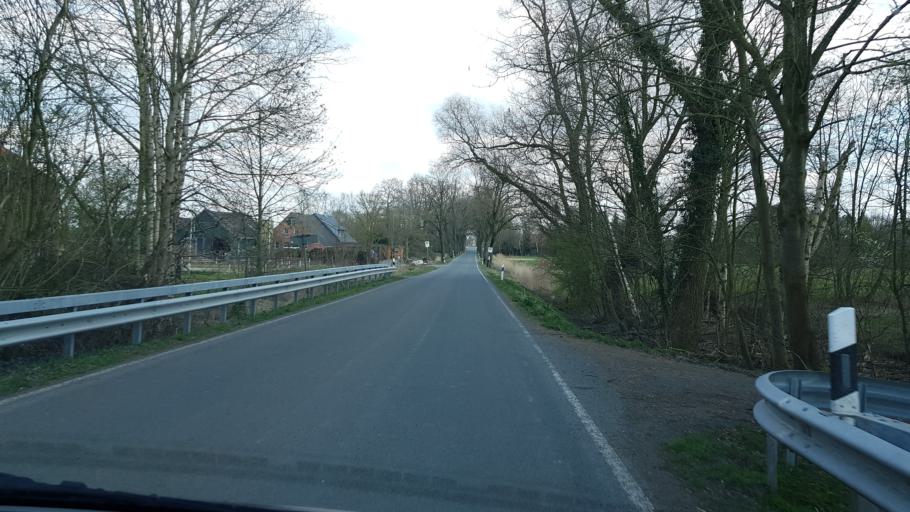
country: DE
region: Lower Saxony
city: Rastede
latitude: 53.3081
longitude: 8.2539
